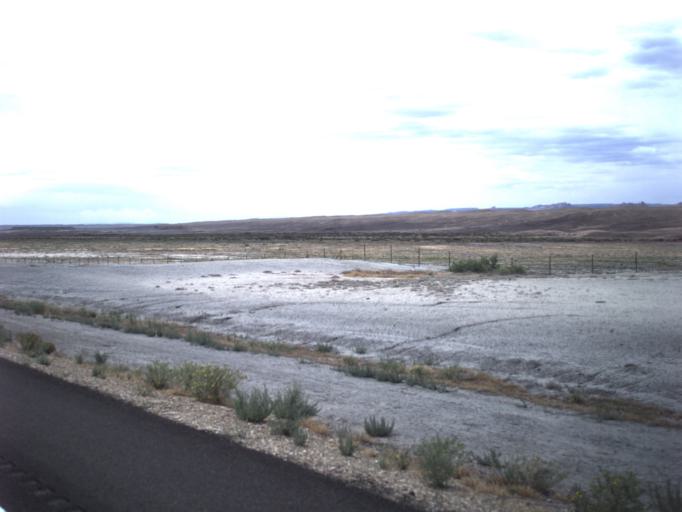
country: US
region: Utah
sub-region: Carbon County
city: East Carbon City
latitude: 39.0694
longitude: -110.3151
